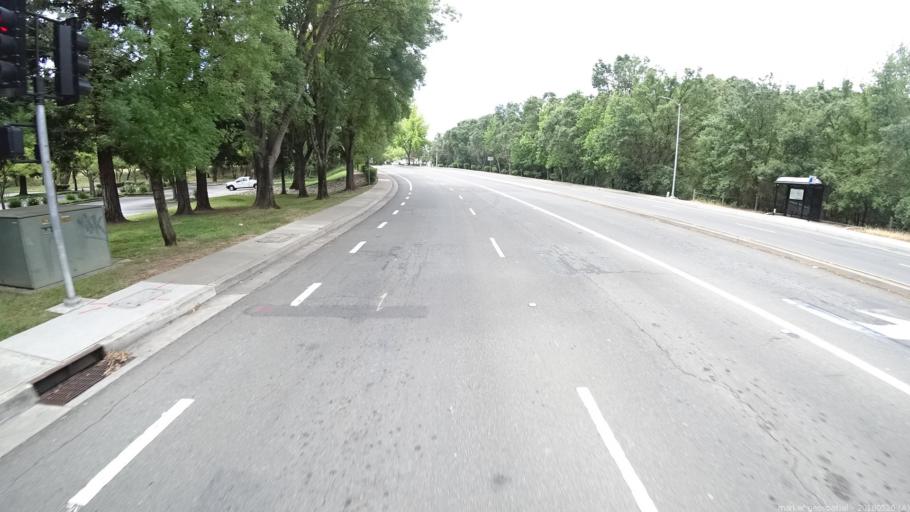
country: US
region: California
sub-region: Yolo County
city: West Sacramento
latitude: 38.6051
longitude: -121.5135
